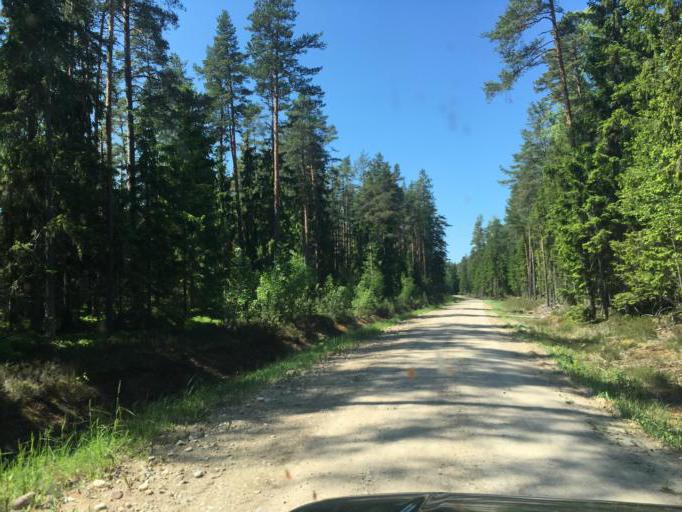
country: LV
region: Talsu Rajons
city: Valdemarpils
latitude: 57.4324
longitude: 22.6920
